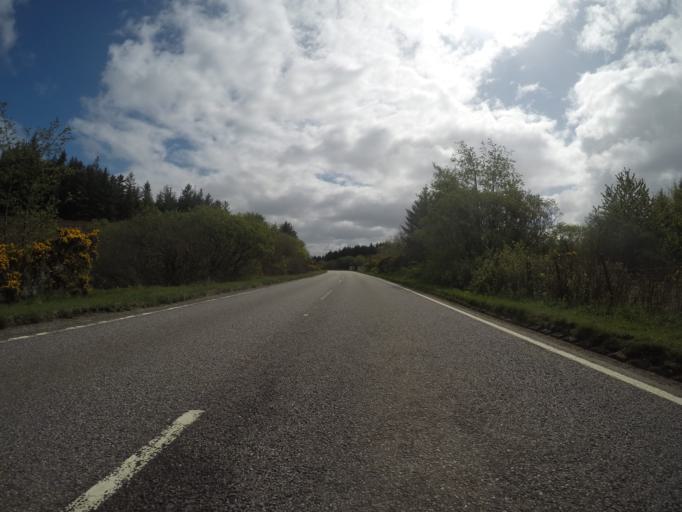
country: GB
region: Scotland
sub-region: Highland
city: Portree
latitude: 57.2464
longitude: -5.9275
